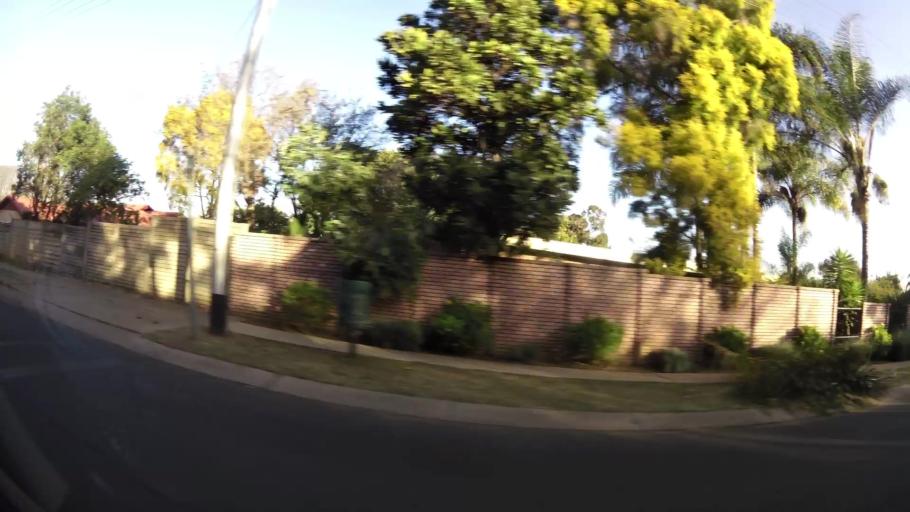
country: ZA
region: Gauteng
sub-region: City of Tshwane Metropolitan Municipality
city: Pretoria
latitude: -25.6993
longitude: 28.2263
